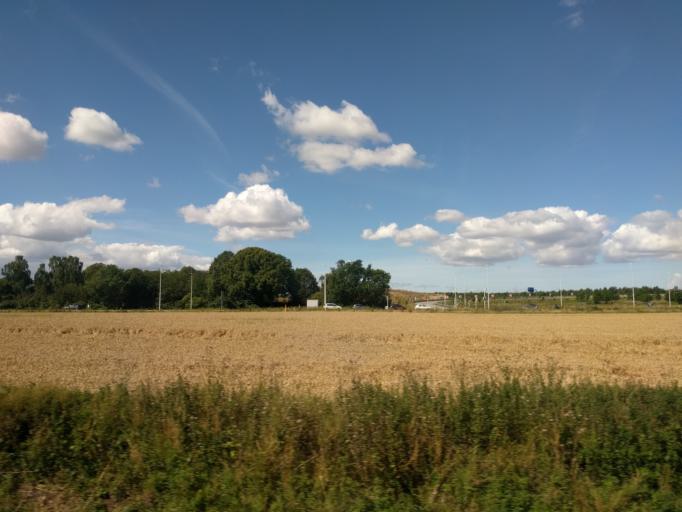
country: DK
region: Zealand
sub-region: Roskilde Kommune
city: Roskilde
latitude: 55.6229
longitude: 12.0598
